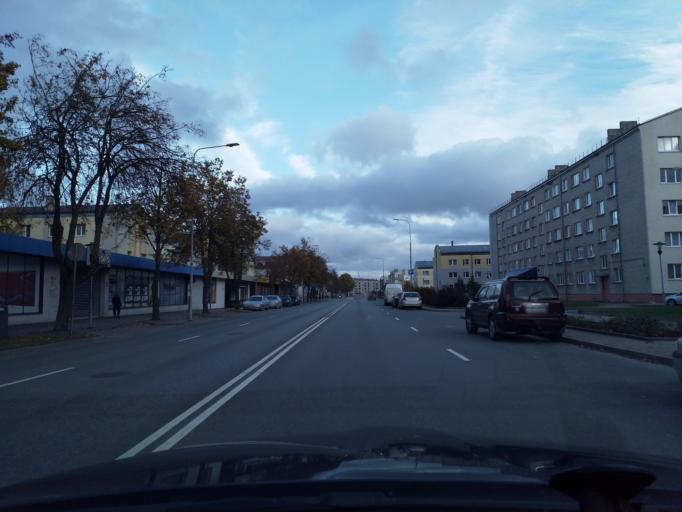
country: LV
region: Ventspils
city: Ventspils
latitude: 57.3896
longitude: 21.5664
